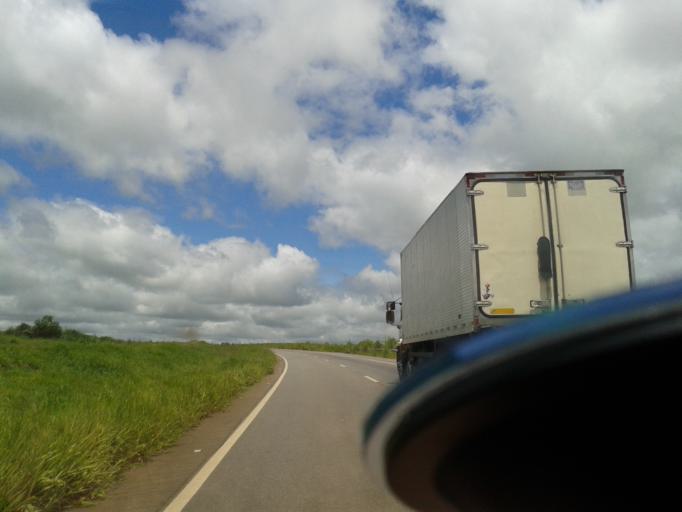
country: BR
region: Goias
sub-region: Itaberai
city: Itaberai
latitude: -16.0761
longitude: -49.7337
